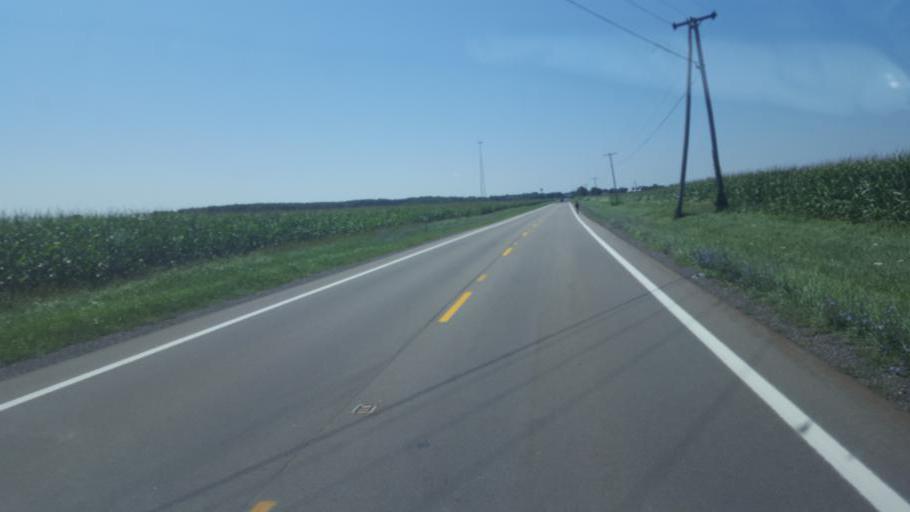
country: US
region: Ohio
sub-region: Delaware County
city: Ashley
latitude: 40.4312
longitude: -82.9525
